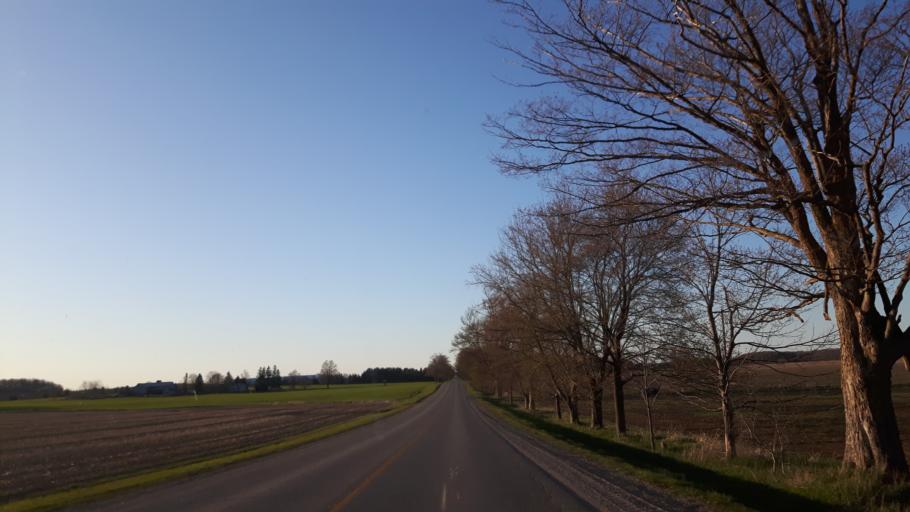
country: CA
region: Ontario
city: Bluewater
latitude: 43.5267
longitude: -81.5432
